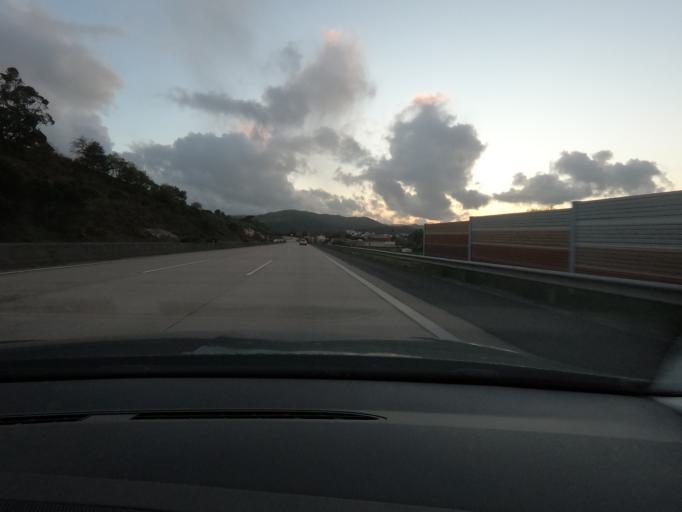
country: PT
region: Lisbon
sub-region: Loures
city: Bucelas
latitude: 38.9009
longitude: -9.1012
